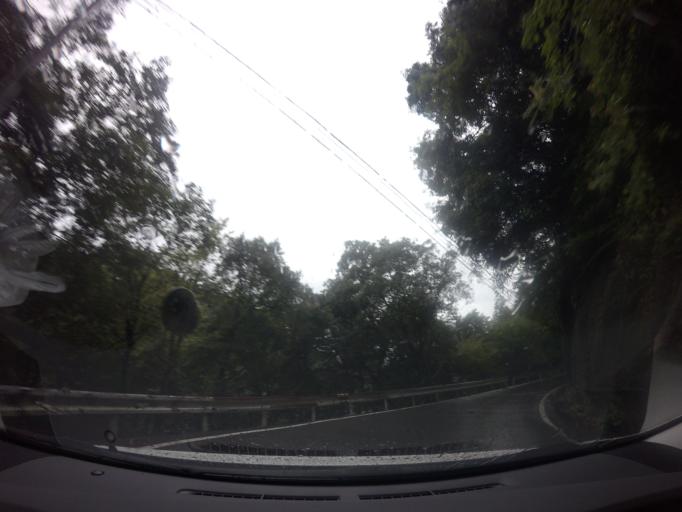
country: JP
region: Wakayama
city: Koya
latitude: 34.0637
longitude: 135.7461
